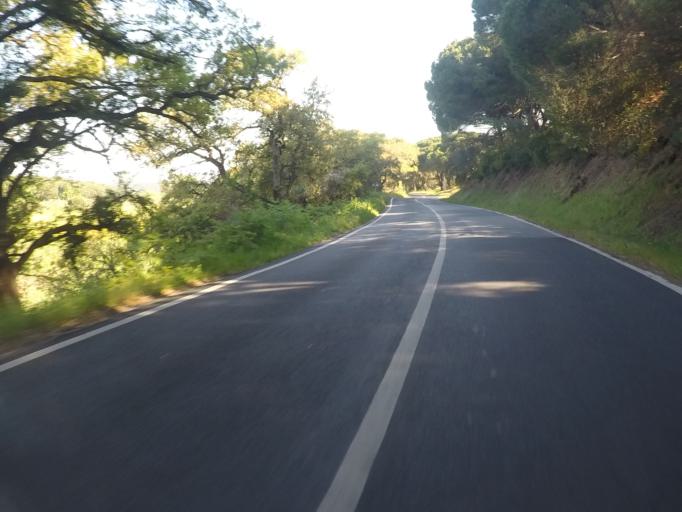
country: PT
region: Setubal
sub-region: Sesimbra
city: Sesimbra
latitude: 38.5065
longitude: -9.1478
